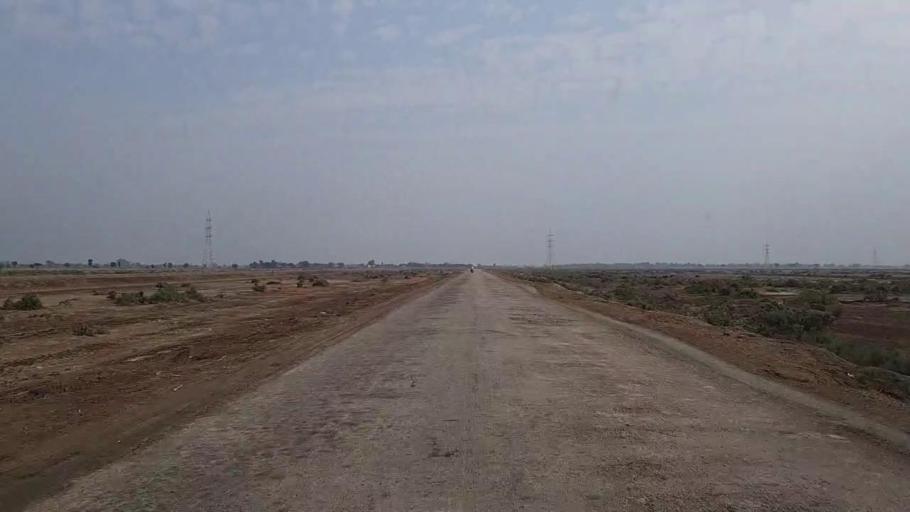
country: PK
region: Sindh
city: Mirpur Khas
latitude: 25.4219
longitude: 69.0244
